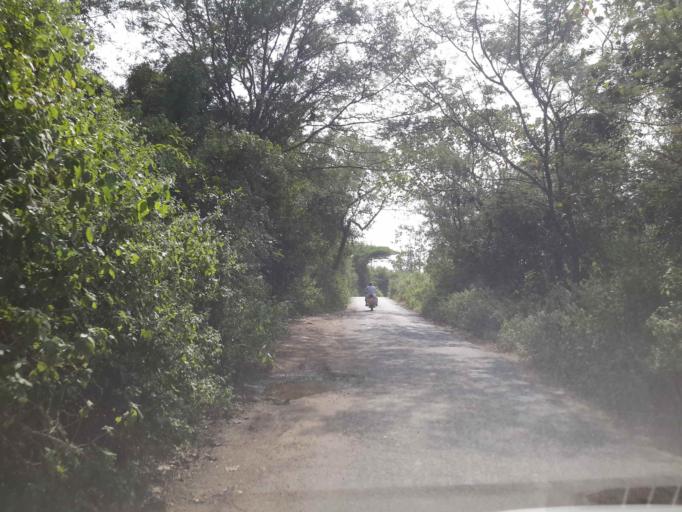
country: IN
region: Tamil Nadu
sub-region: Coimbatore
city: Mettupalayam
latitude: 11.2833
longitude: 76.8894
